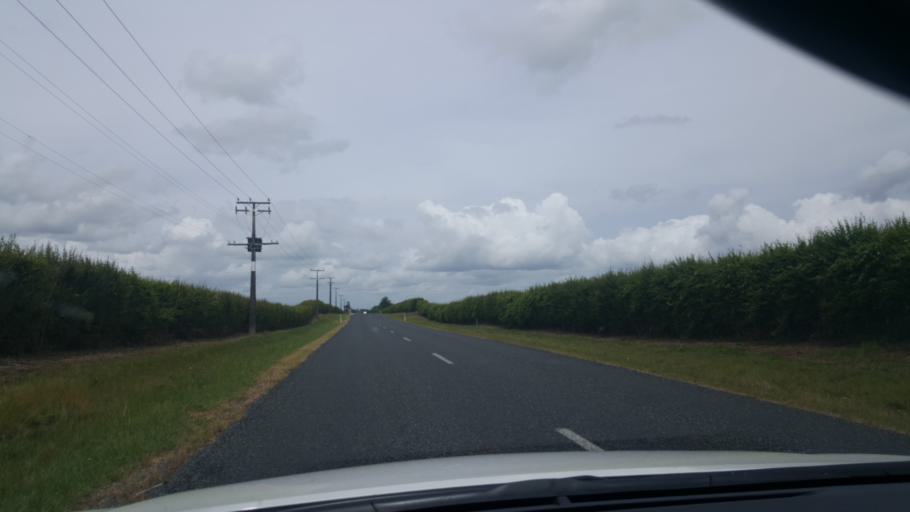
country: NZ
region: Waikato
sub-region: Matamata-Piako District
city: Matamata
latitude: -37.8781
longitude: 175.7283
